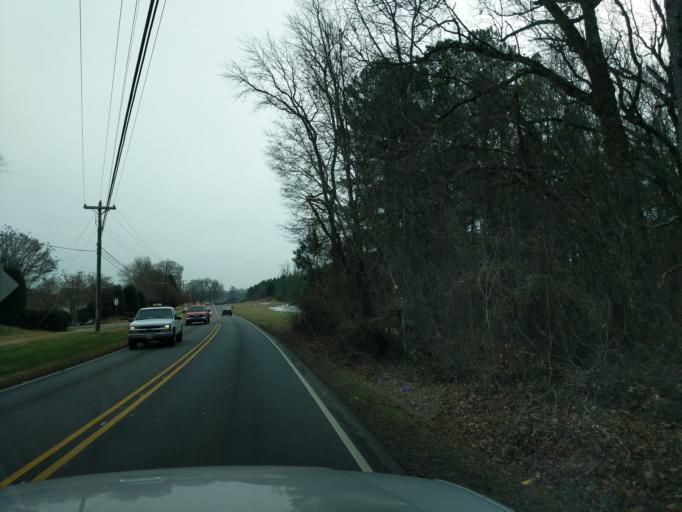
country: US
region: North Carolina
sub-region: Mecklenburg County
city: Charlotte
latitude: 35.3055
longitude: -80.8666
